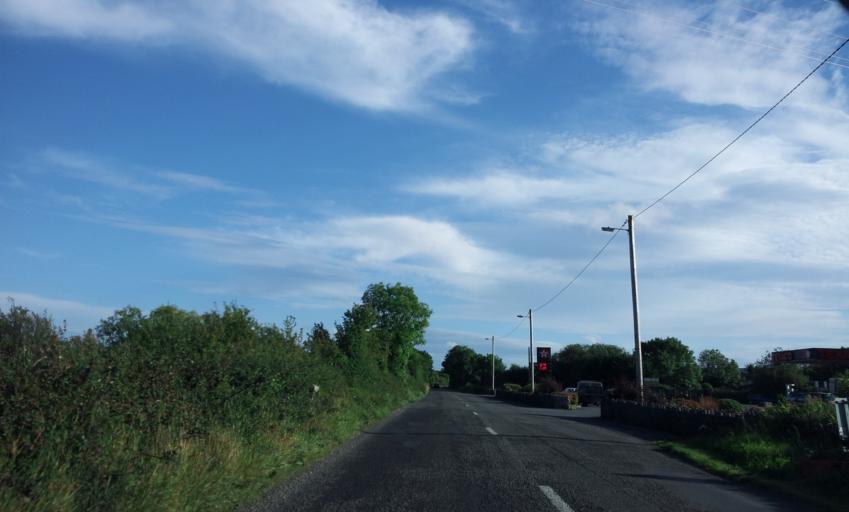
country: IE
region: Munster
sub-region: An Clar
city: Ennis
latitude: 52.9385
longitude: -9.0614
